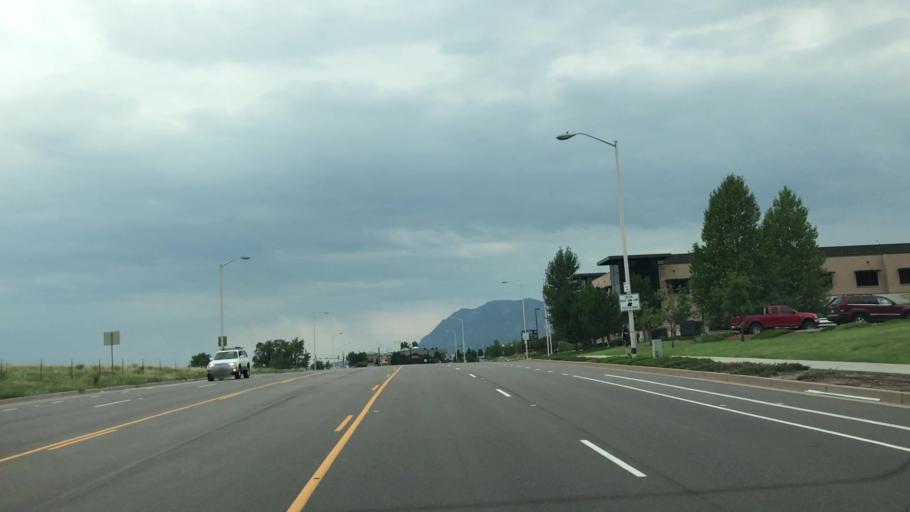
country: US
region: Colorado
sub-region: El Paso County
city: Colorado Springs
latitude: 38.8818
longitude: -104.8477
